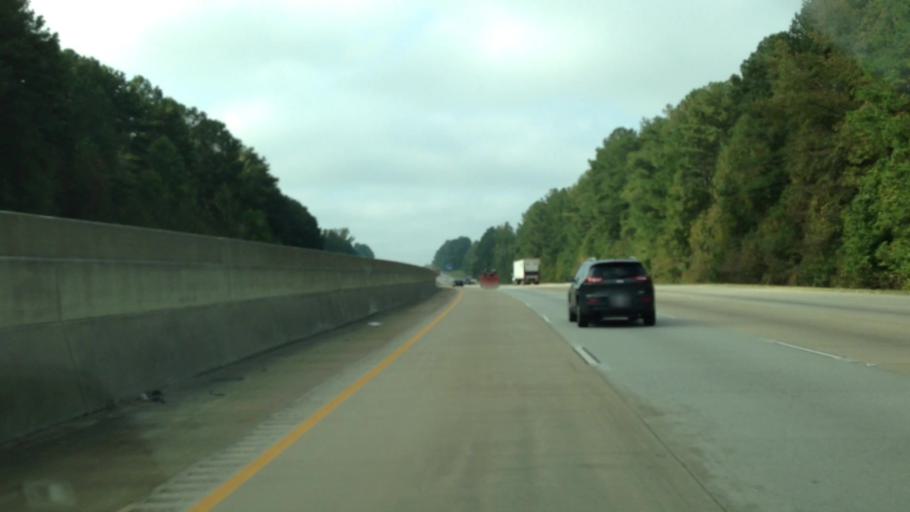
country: US
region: Georgia
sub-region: Coweta County
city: Newnan
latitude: 33.4257
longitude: -84.7249
